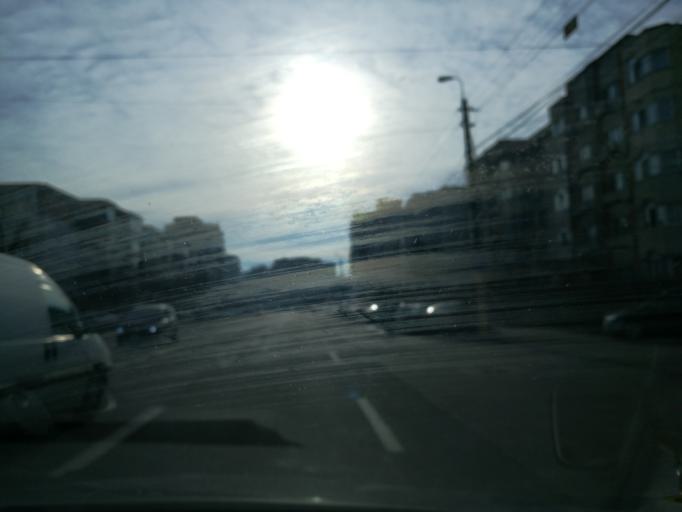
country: RO
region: Constanta
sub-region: Municipiul Constanta
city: Constanta
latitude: 44.1748
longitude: 28.6121
